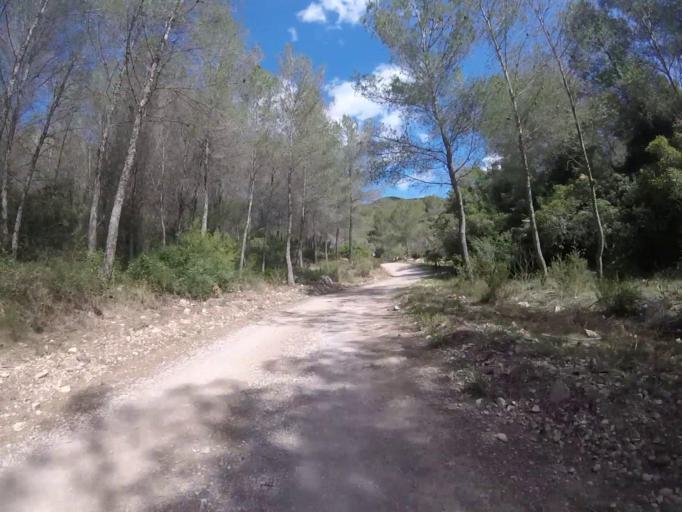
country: ES
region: Valencia
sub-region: Provincia de Castello
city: Santa Magdalena de Pulpis
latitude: 40.3180
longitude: 0.3292
